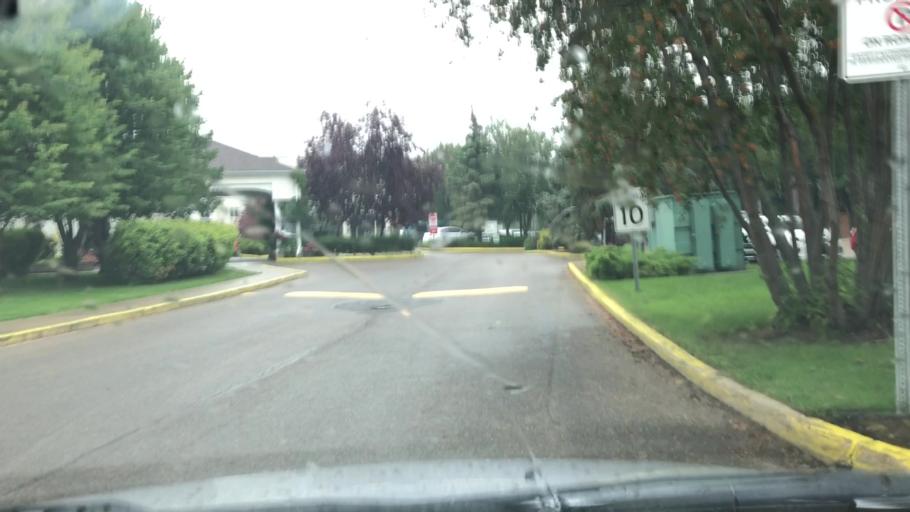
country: CA
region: Alberta
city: St. Albert
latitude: 53.6408
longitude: -113.6351
